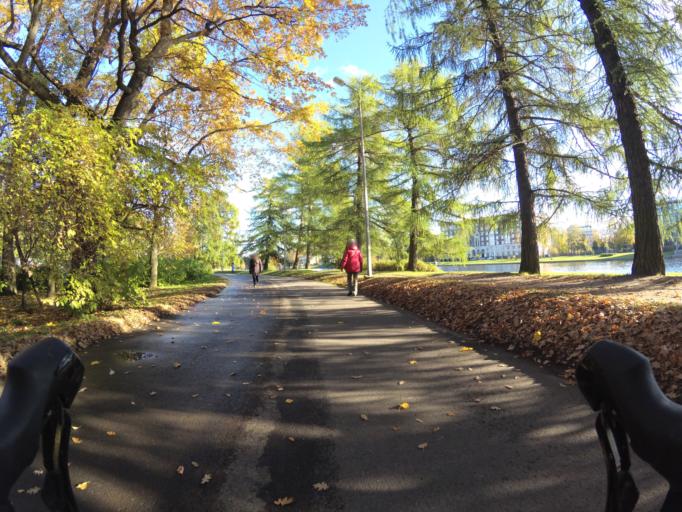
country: RU
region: Leningrad
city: Krestovskiy ostrov
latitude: 59.9755
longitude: 30.2667
